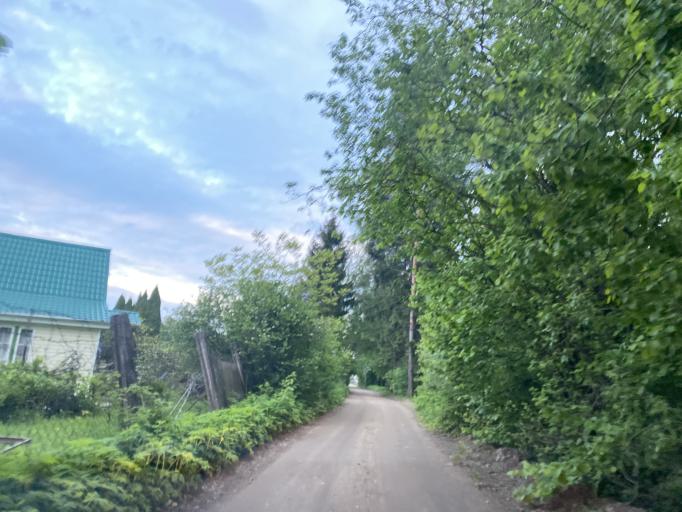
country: BY
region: Minsk
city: Rudzyensk
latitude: 53.6073
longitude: 27.7899
